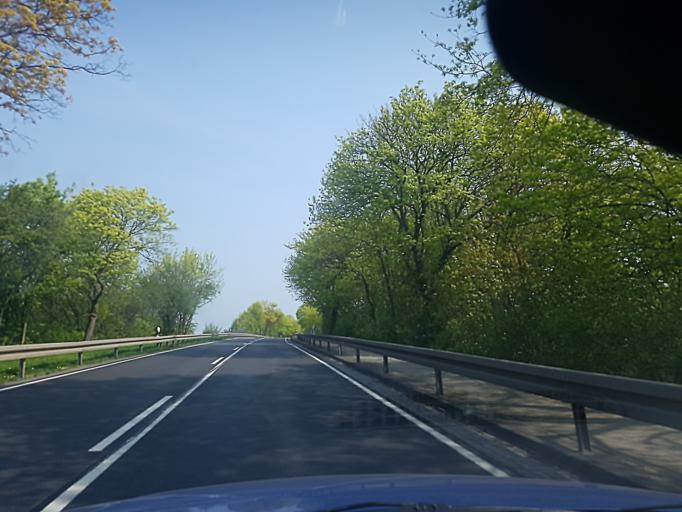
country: DE
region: Saxony
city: Torgau
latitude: 51.5670
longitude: 13.0234
